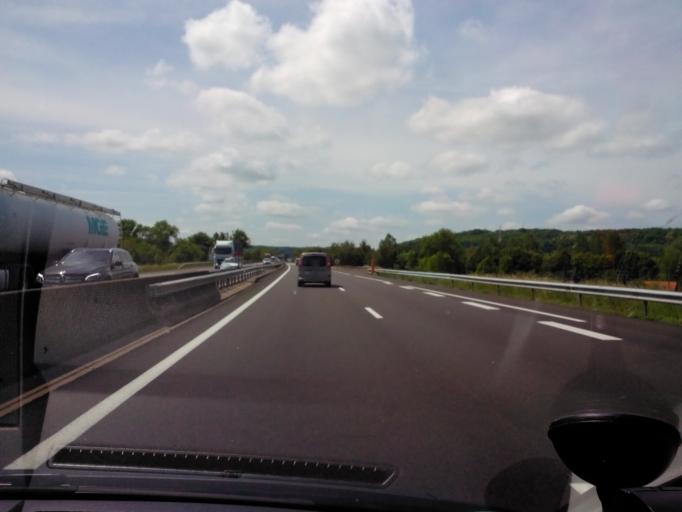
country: FR
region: Champagne-Ardenne
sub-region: Departement de la Haute-Marne
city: Rolampont
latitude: 47.9391
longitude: 5.2957
